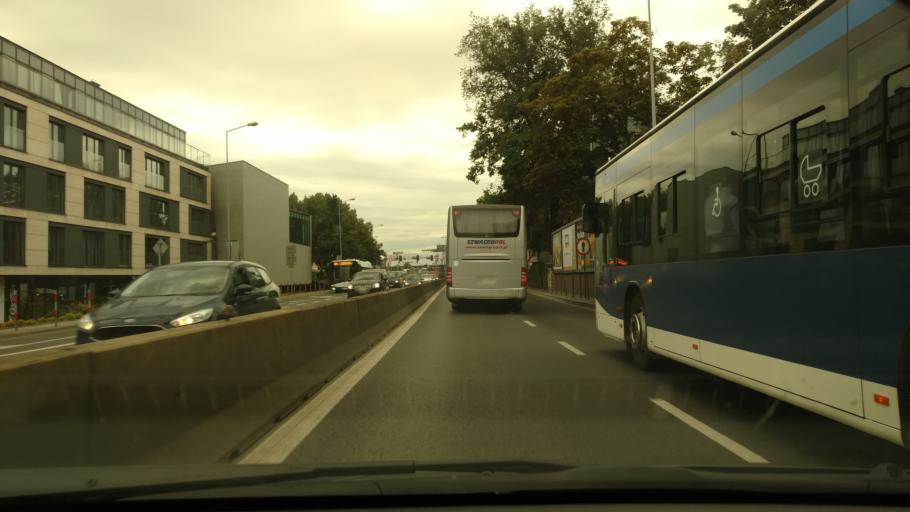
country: PL
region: Lesser Poland Voivodeship
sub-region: Krakow
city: Krakow
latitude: 50.0518
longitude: 19.9301
